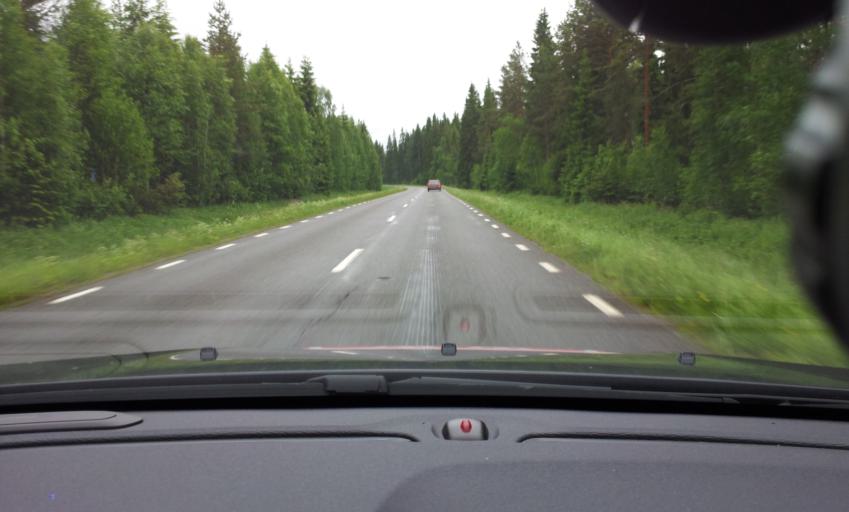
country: SE
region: Jaemtland
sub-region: Stroemsunds Kommun
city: Stroemsund
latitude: 63.4731
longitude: 15.4480
